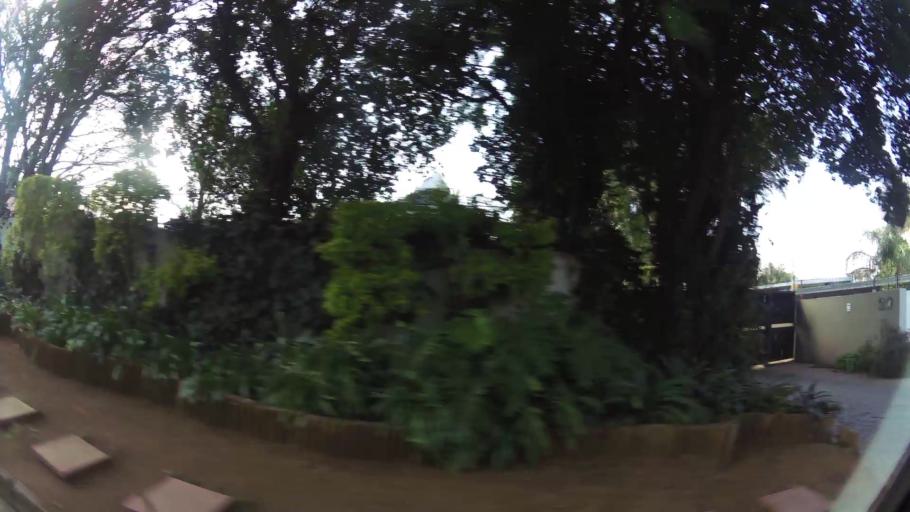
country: ZA
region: Gauteng
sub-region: Ekurhuleni Metropolitan Municipality
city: Boksburg
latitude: -26.1941
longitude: 28.2368
